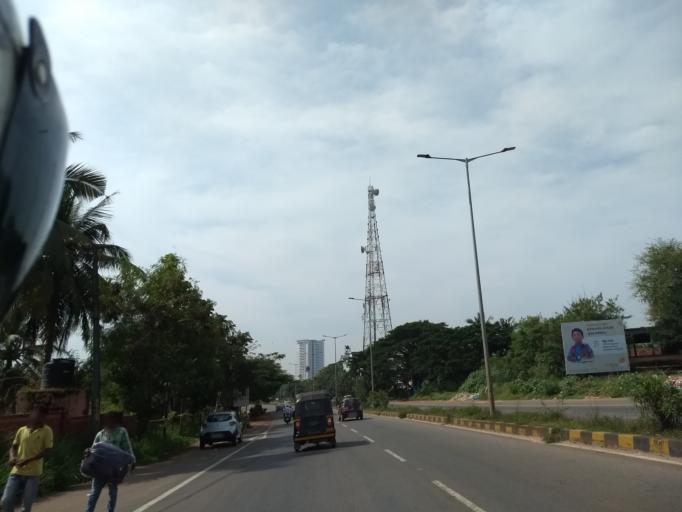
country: IN
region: Karnataka
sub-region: Dakshina Kannada
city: Mangalore
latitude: 12.8884
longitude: 74.8601
